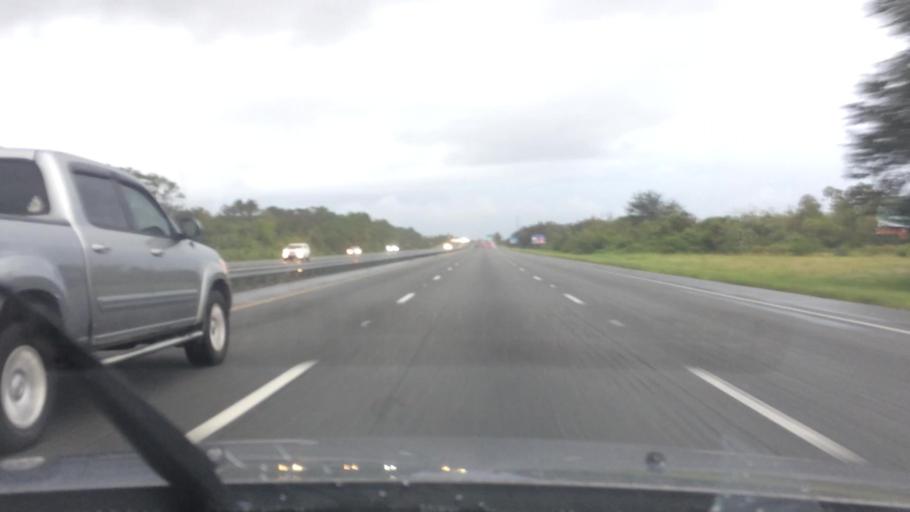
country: US
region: Florida
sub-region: Volusia County
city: Ormond-by-the-Sea
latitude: 29.3249
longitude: -81.1313
